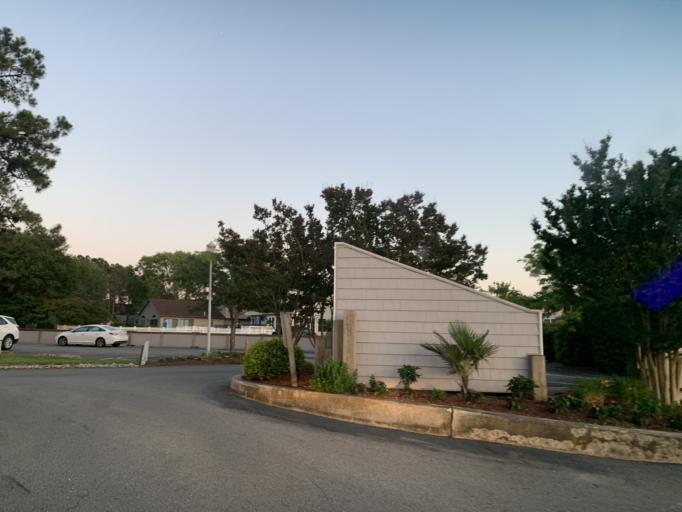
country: US
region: Delaware
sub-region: Sussex County
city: Bethany Beach
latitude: 38.4515
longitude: -75.0618
